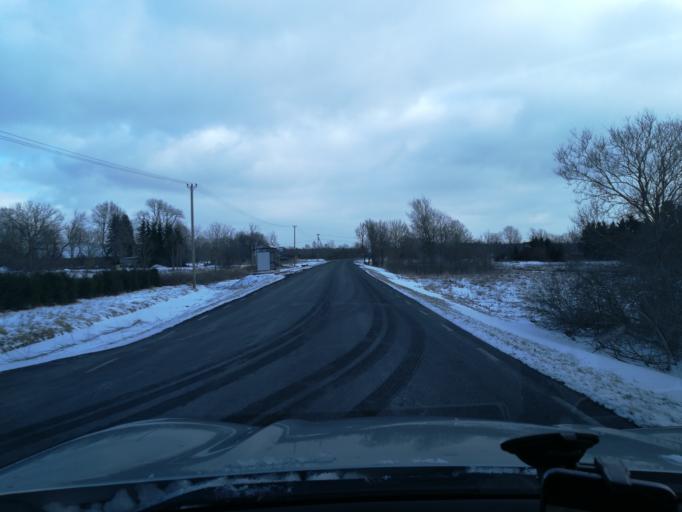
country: EE
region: Harju
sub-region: Harku vald
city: Tabasalu
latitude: 59.4271
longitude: 24.4161
